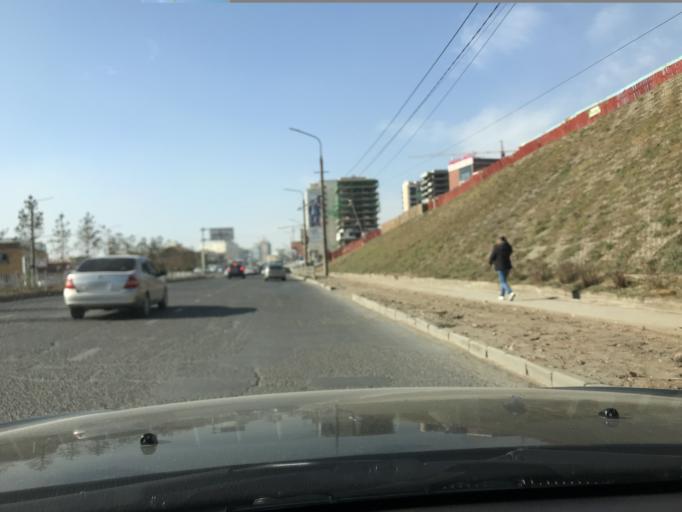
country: MN
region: Ulaanbaatar
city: Ulaanbaatar
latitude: 47.9261
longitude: 106.8987
